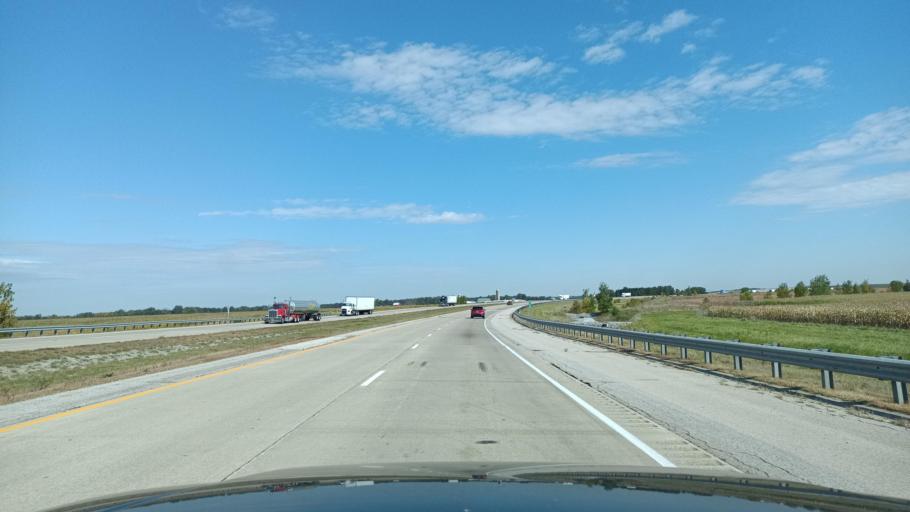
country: US
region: Indiana
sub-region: Allen County
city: Woodburn
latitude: 41.1313
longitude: -84.8768
